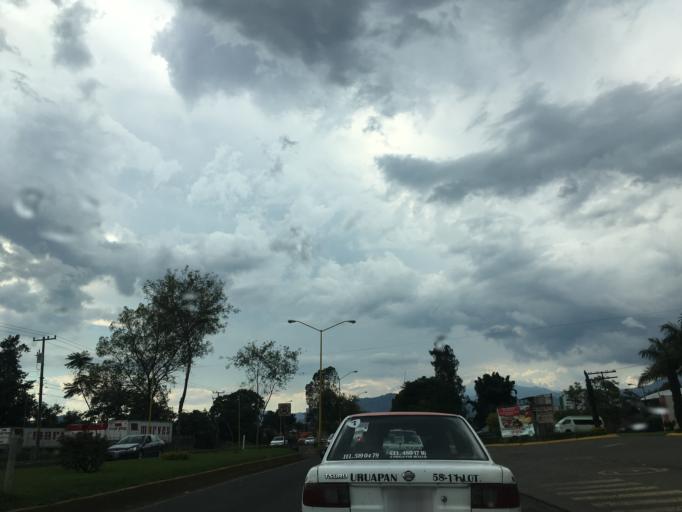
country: MX
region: Michoacan
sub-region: Uruapan
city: Uruapan
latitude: 19.4225
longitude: -102.0329
